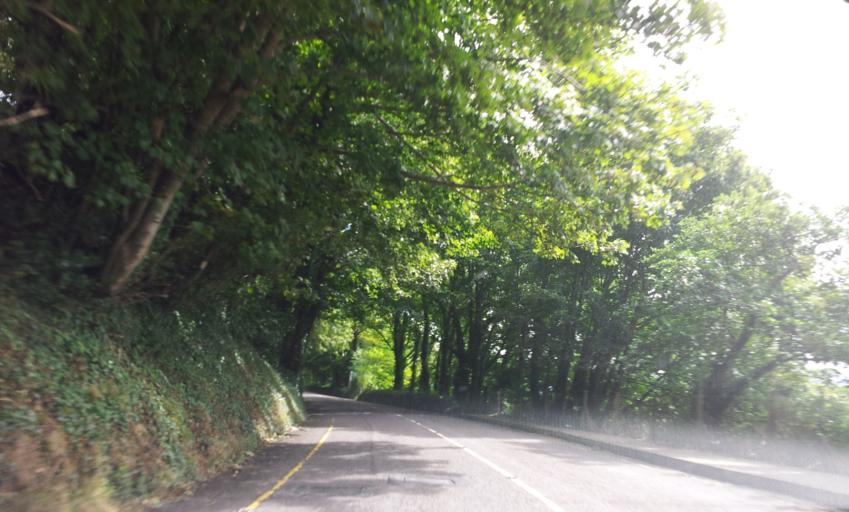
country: IE
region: Munster
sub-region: Ciarrai
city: Killorglin
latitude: 52.1042
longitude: -9.7787
